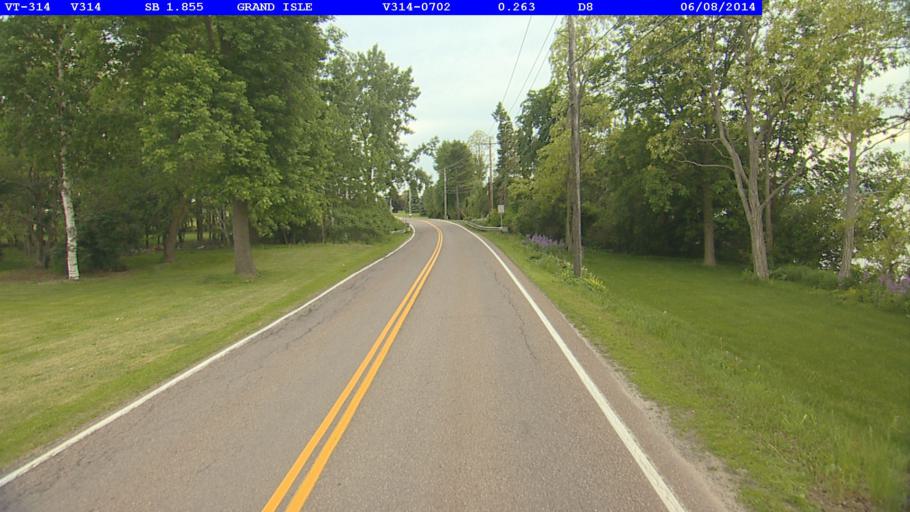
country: US
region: New York
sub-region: Clinton County
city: Cumberland Head
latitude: 44.6812
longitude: -73.3477
